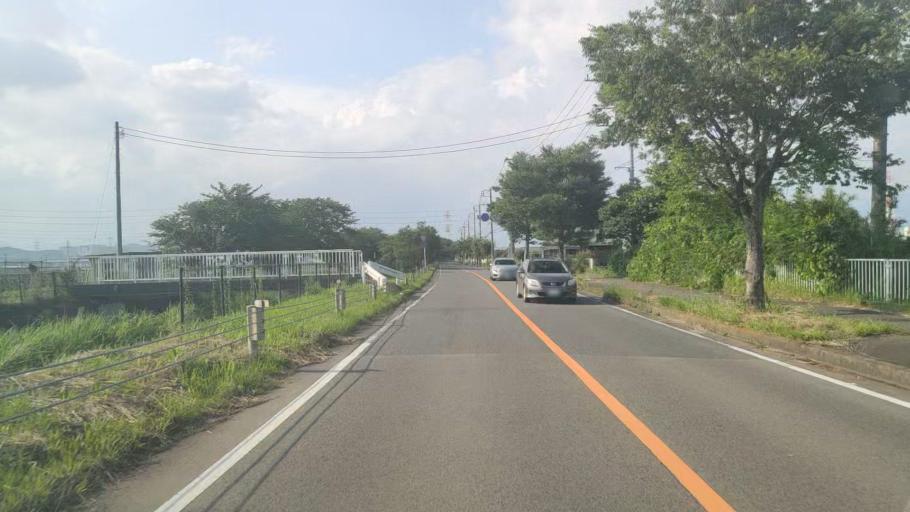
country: JP
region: Kanagawa
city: Isehara
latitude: 35.3921
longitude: 139.3379
